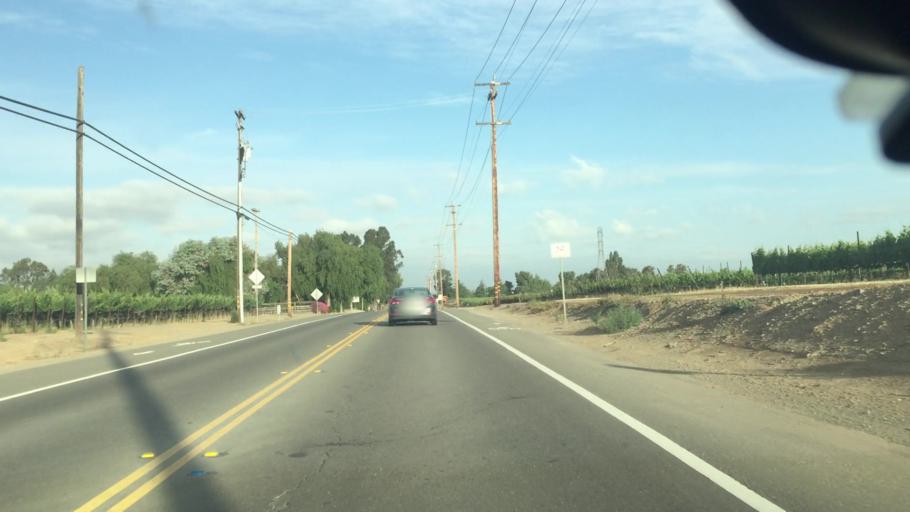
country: US
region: California
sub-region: Alameda County
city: Livermore
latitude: 37.6651
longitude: -121.7279
